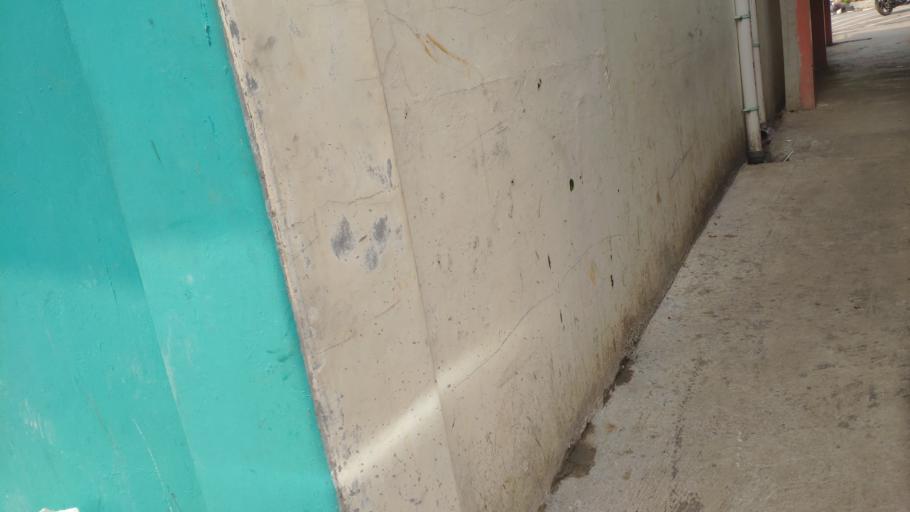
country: ID
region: West Java
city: Depok
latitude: -6.3461
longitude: 106.8142
